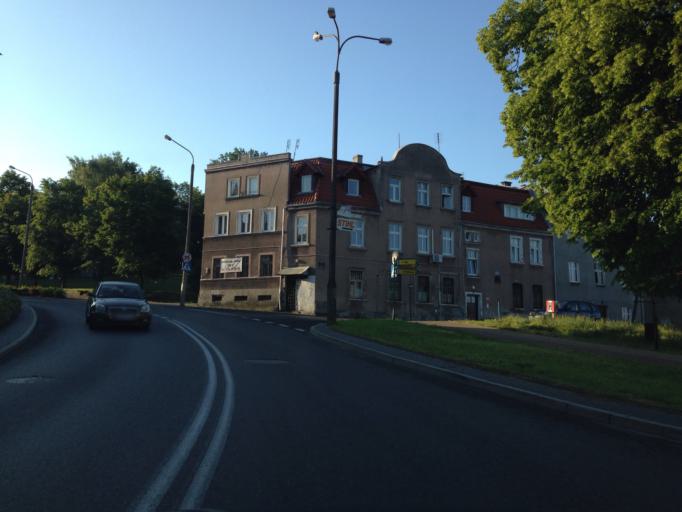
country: PL
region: Pomeranian Voivodeship
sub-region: Powiat kwidzynski
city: Kwidzyn
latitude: 53.7342
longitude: 18.9190
